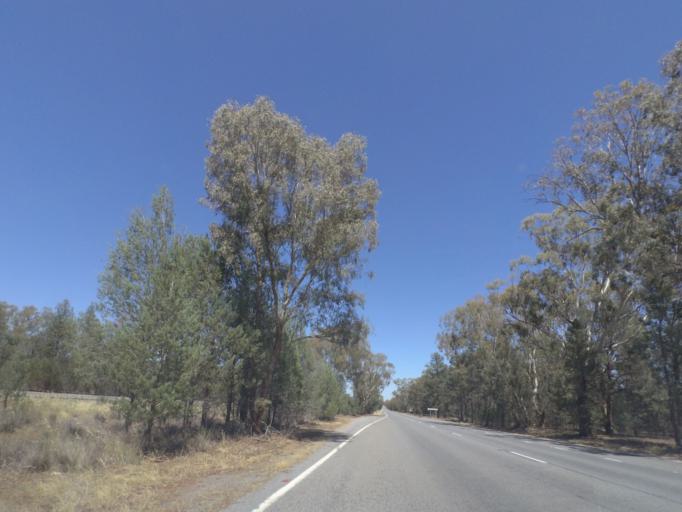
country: AU
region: New South Wales
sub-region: Narrandera
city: Narrandera
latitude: -34.7366
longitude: 146.5951
